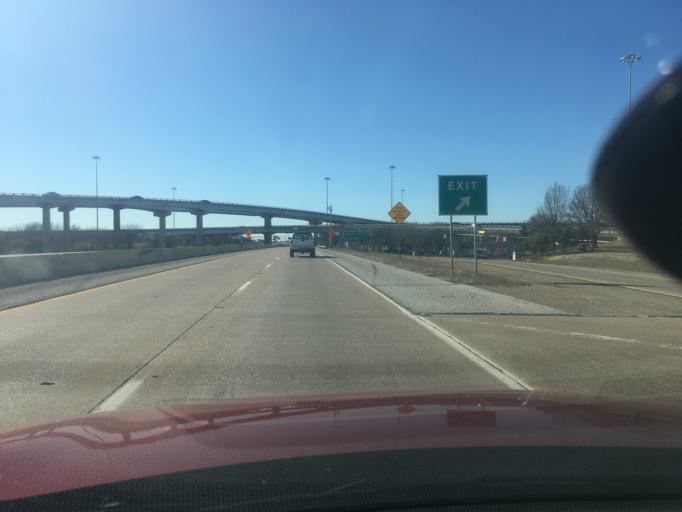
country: US
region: Texas
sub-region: Dallas County
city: Duncanville
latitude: 32.6558
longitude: -96.8762
